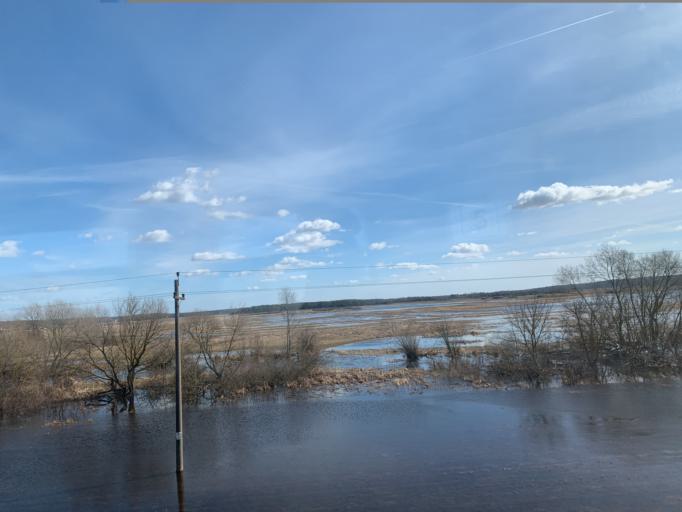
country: BY
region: Minsk
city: Stowbtsy
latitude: 53.4702
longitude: 26.7348
